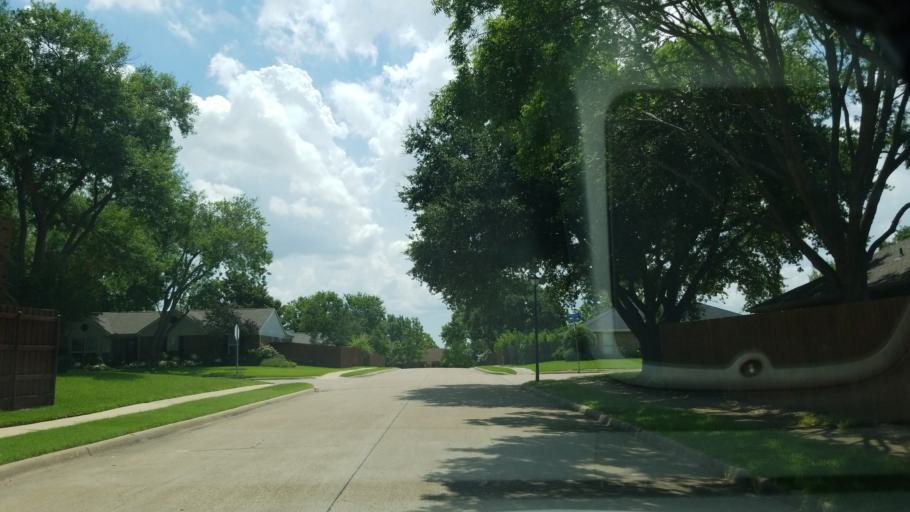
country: US
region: Texas
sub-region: Dallas County
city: Coppell
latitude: 32.9642
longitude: -96.9626
